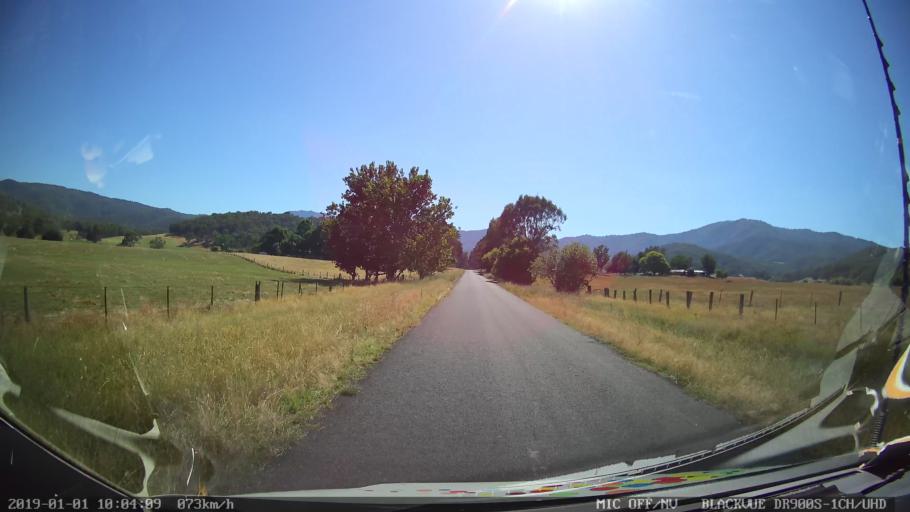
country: AU
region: New South Wales
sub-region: Snowy River
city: Jindabyne
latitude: -36.1768
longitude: 148.1188
